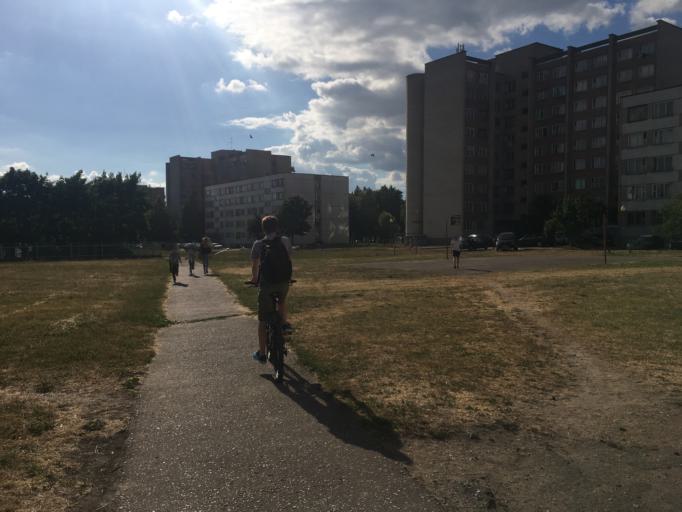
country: BY
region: Grodnenskaya
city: Hrodna
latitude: 53.7093
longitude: 23.8100
